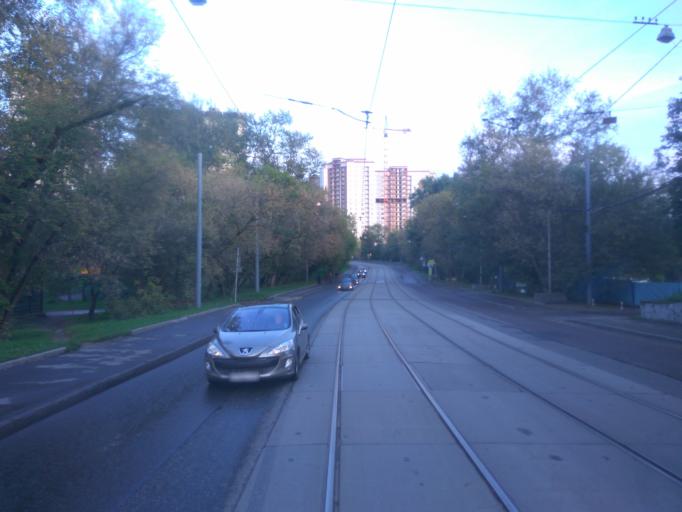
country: RU
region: Moskovskaya
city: Bogorodskoye
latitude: 55.8141
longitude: 37.6955
